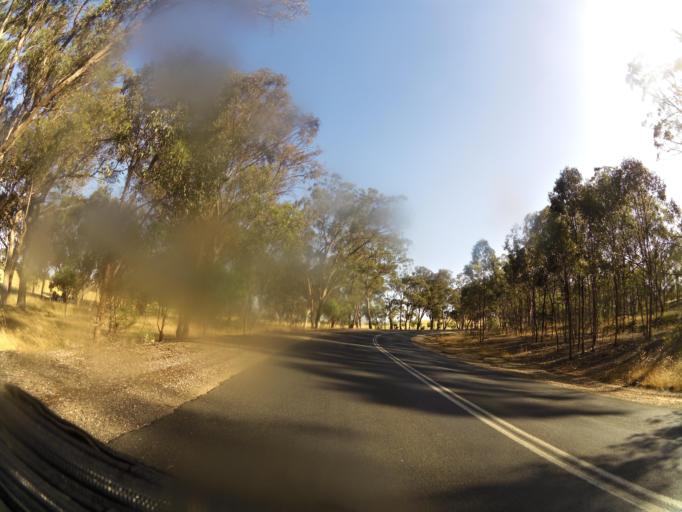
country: AU
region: Victoria
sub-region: Murrindindi
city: Kinglake West
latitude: -37.0076
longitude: 145.1241
